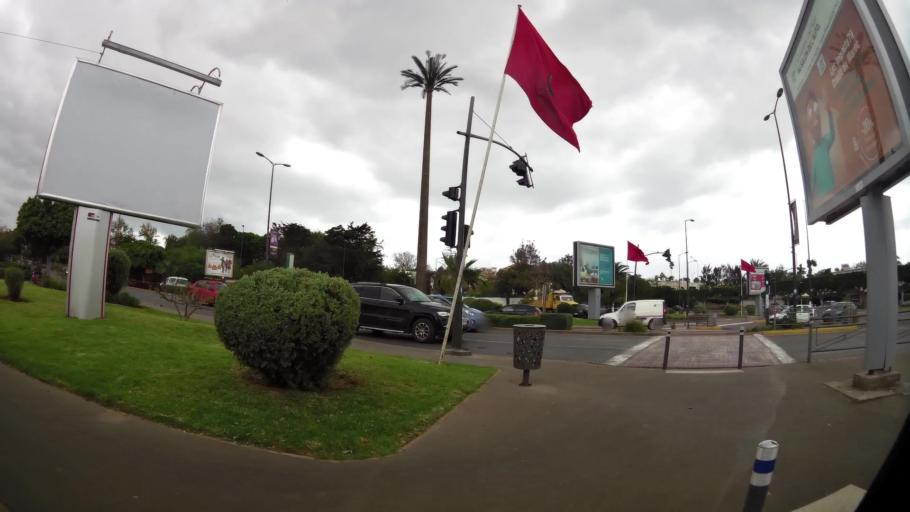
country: MA
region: Grand Casablanca
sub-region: Casablanca
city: Casablanca
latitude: 33.5819
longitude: -7.6618
